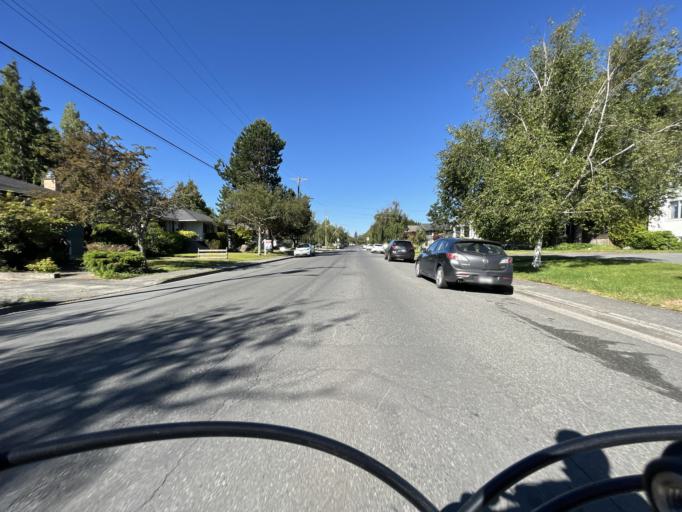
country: CA
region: British Columbia
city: Victoria
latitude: 48.4171
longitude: -123.3330
